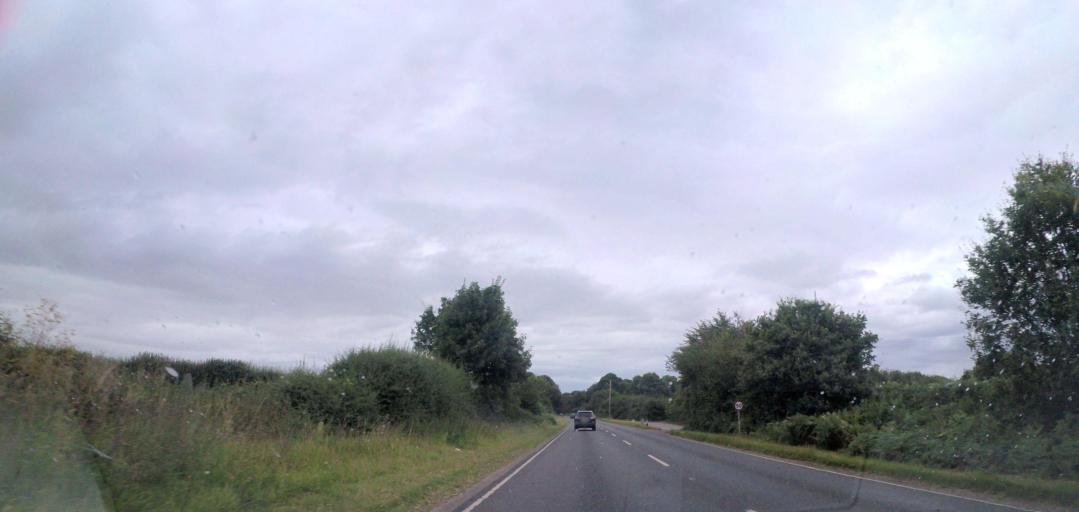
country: GB
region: England
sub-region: Norfolk
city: Spixworth
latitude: 52.6908
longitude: 1.3359
